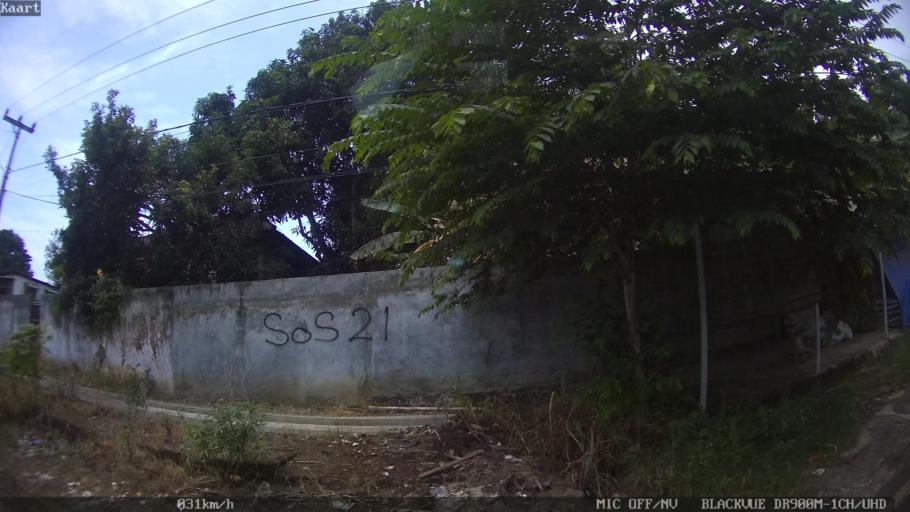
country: ID
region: Lampung
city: Bandarlampung
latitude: -5.4091
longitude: 105.2242
